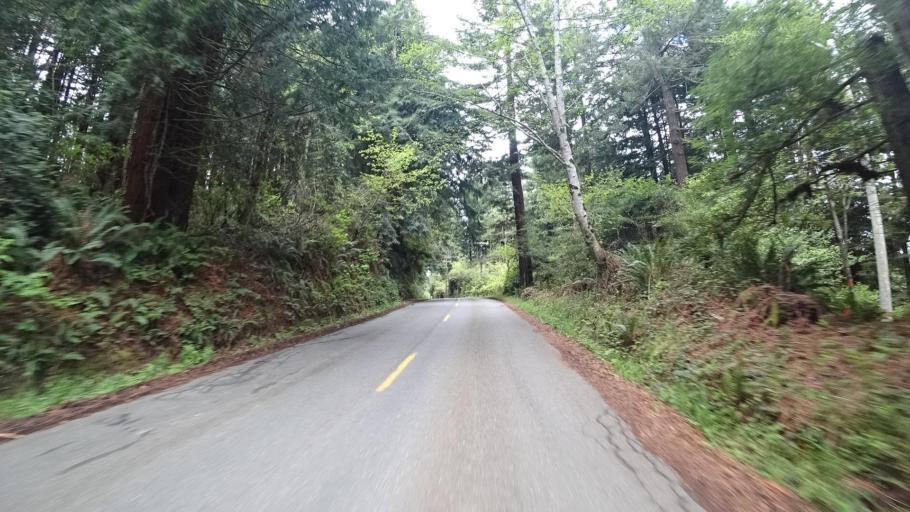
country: US
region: California
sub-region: Humboldt County
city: Bayside
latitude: 40.7977
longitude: -124.0472
